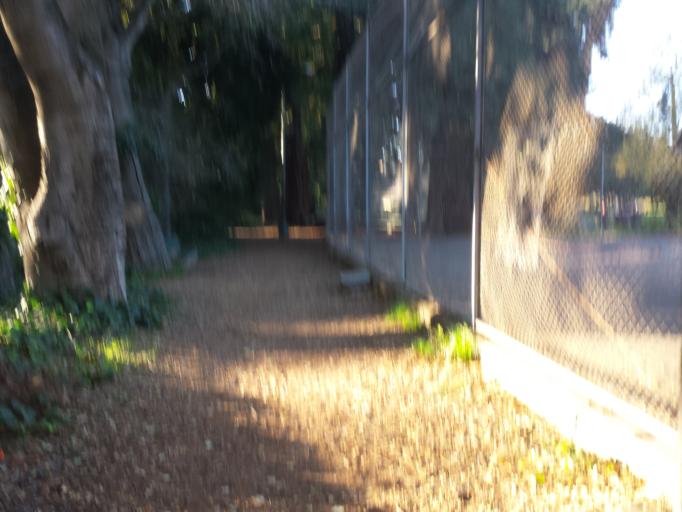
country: US
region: California
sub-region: Alameda County
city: Piedmont
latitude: 37.8034
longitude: -122.2155
